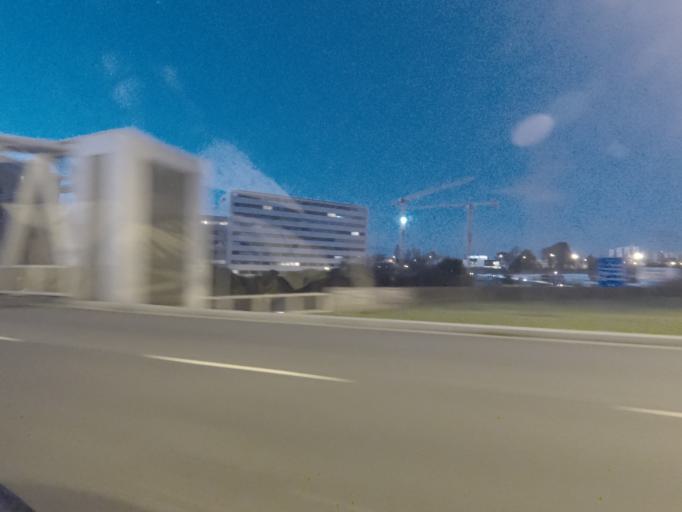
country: PT
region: Porto
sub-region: Matosinhos
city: Senhora da Hora
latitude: 41.1654
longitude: -8.6443
